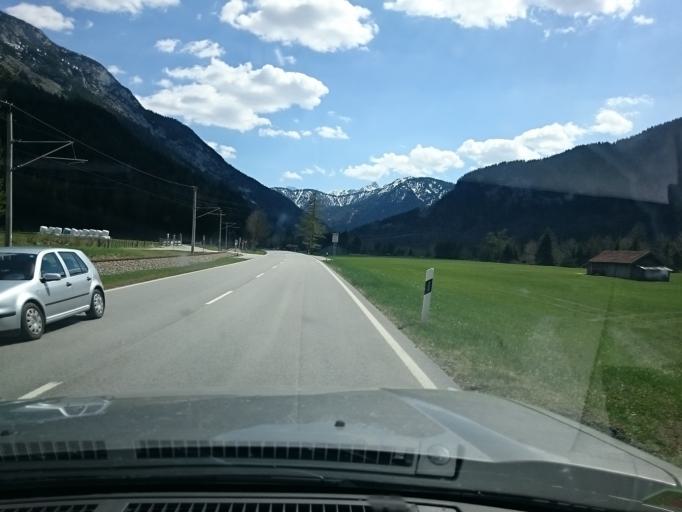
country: AT
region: Tyrol
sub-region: Politischer Bezirk Innsbruck Land
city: Scharnitz
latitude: 47.4110
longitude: 11.2584
